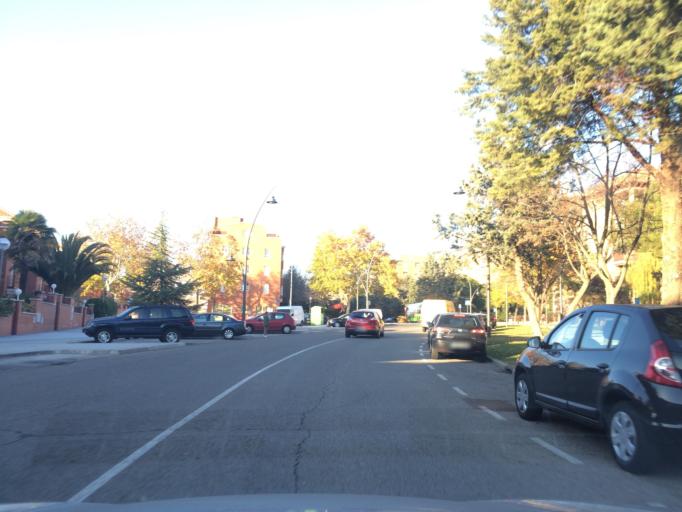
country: ES
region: Madrid
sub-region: Provincia de Madrid
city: Tres Cantos
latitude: 40.5929
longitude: -3.7033
